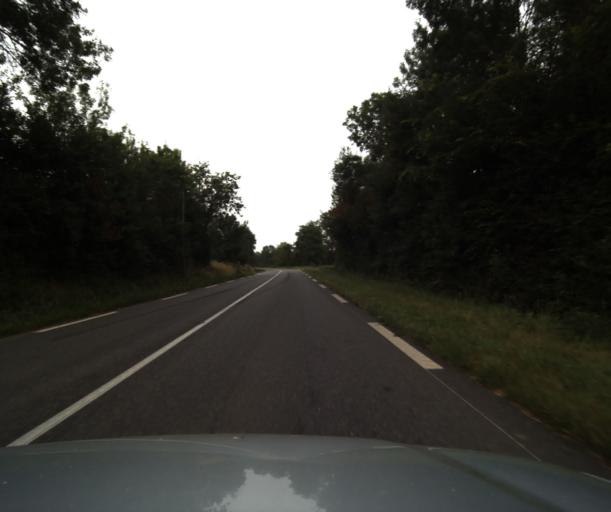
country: FR
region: Midi-Pyrenees
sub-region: Departement du Gers
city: Gimont
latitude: 43.7074
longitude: 0.8530
